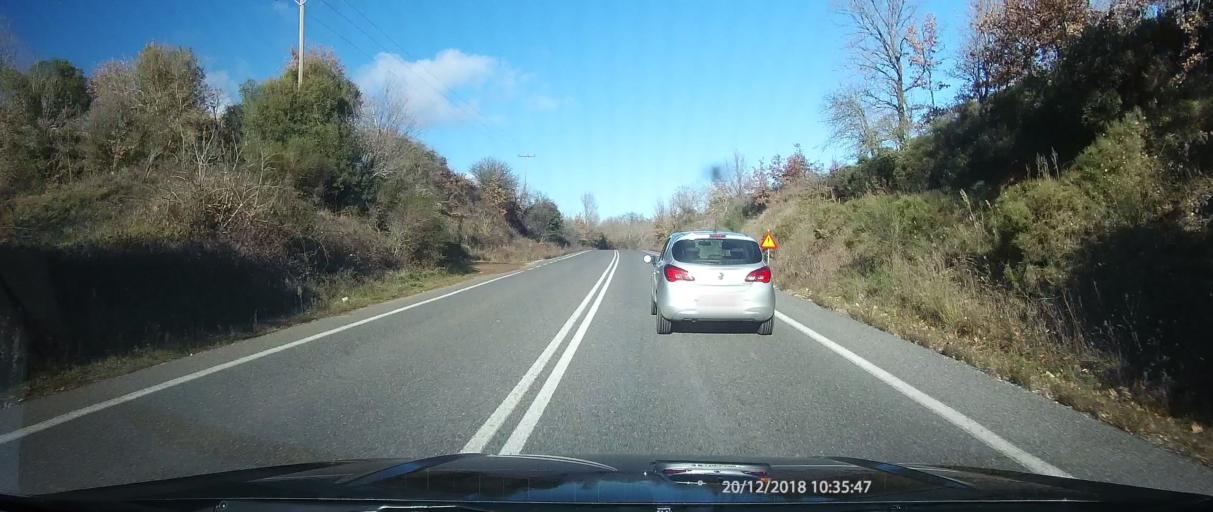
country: GR
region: Peloponnese
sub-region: Nomos Lakonias
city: Kariai
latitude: 37.3589
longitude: 22.4065
